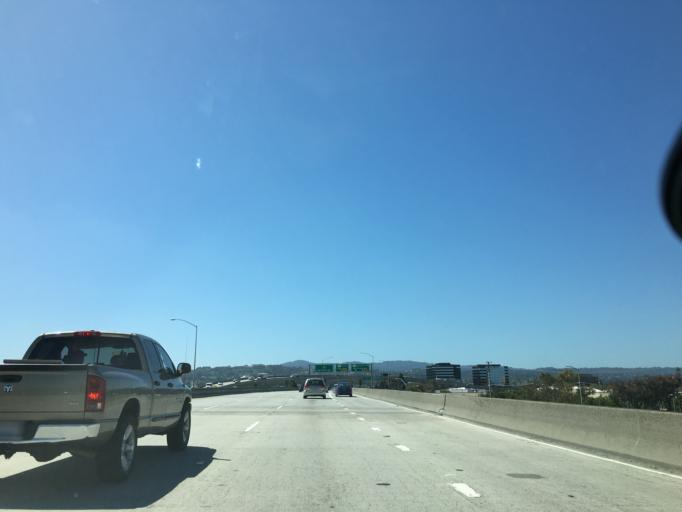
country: US
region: California
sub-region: San Mateo County
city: Foster City
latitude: 37.5546
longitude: -122.2901
